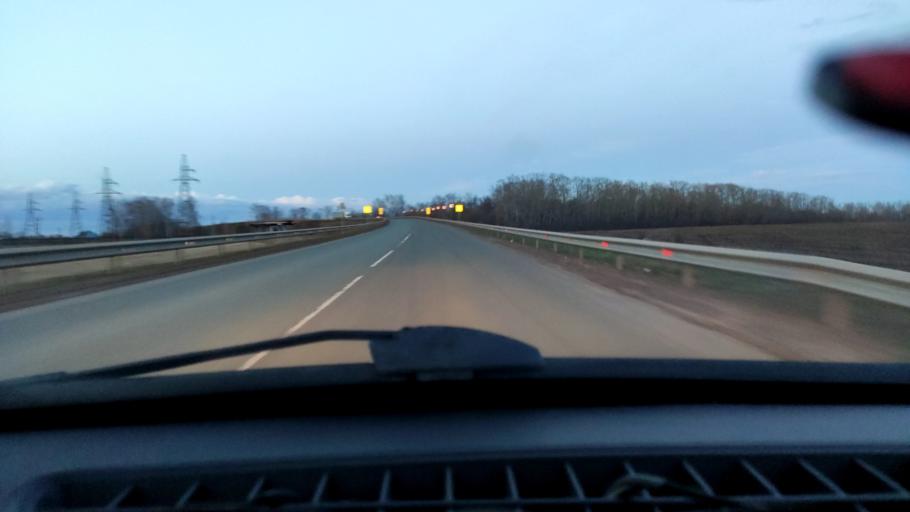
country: RU
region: Bashkortostan
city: Ulukulevo
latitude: 54.4176
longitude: 56.3465
